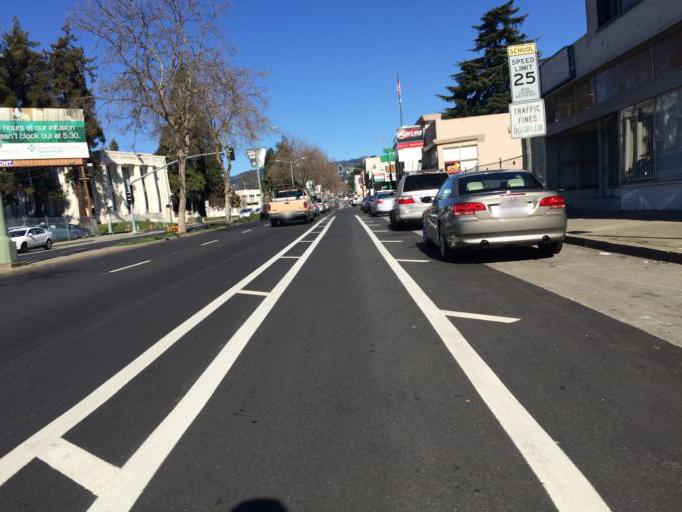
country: US
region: California
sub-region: Alameda County
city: Piedmont
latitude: 37.8306
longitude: -122.2547
